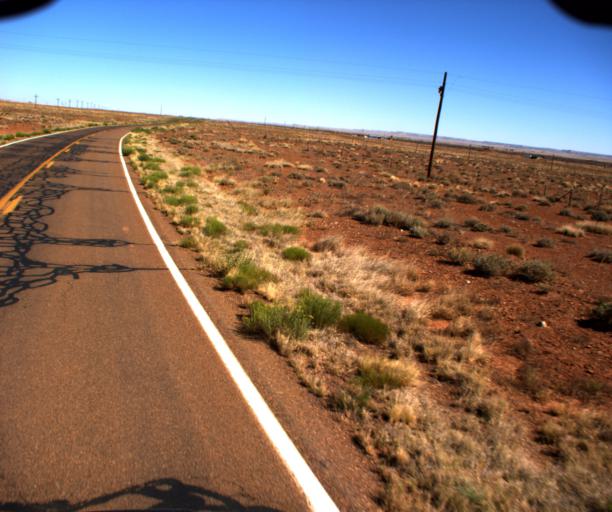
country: US
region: Arizona
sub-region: Coconino County
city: LeChee
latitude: 35.2791
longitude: -110.9812
